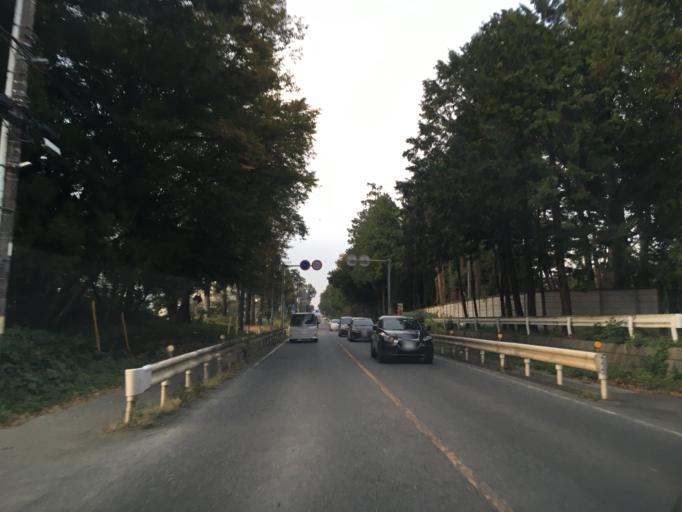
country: JP
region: Saitama
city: Sayama
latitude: 35.8886
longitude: 139.3784
